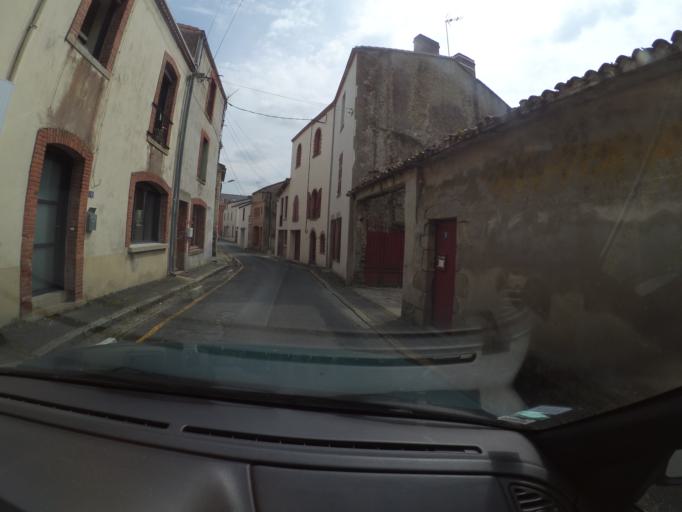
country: FR
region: Pays de la Loire
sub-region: Departement de la Loire-Atlantique
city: Clisson
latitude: 47.0878
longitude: -1.2793
